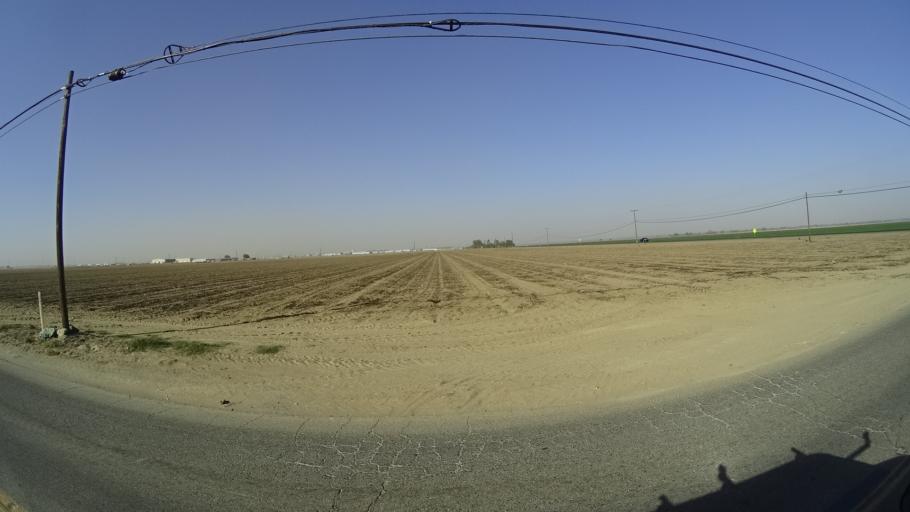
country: US
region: California
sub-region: Yolo County
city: Woodland
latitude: 38.7346
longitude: -121.7304
